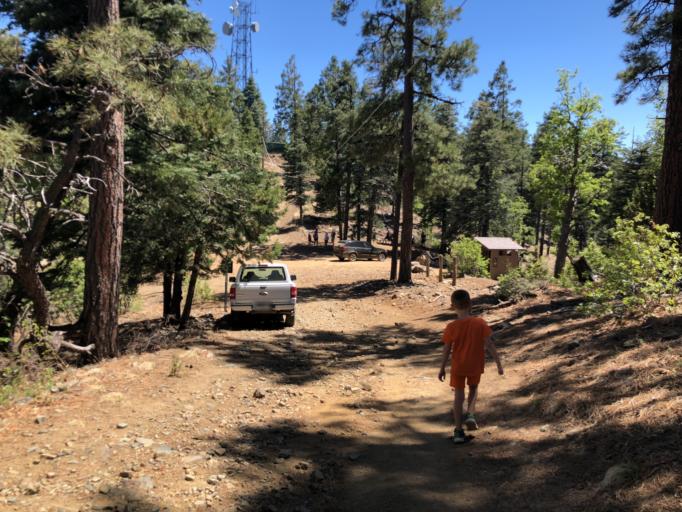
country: US
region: Arizona
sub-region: Yavapai County
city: Prescott
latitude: 34.4627
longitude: -112.4036
